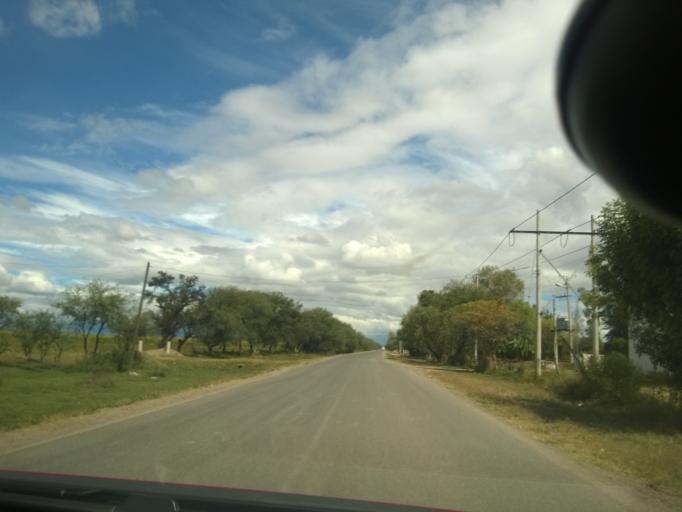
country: MX
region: Guanajuato
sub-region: Leon
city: Plan Guanajuato (La Sandia)
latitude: 20.9618
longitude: -101.6420
